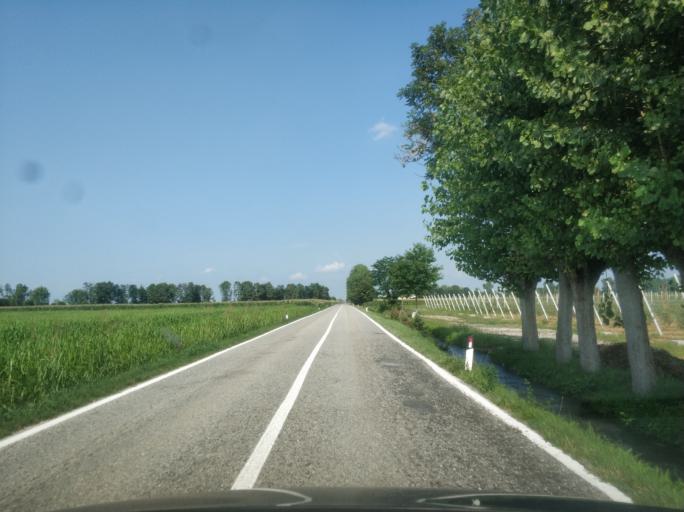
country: IT
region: Piedmont
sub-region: Provincia di Cuneo
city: Roata Rossi
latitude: 44.4609
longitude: 7.4952
